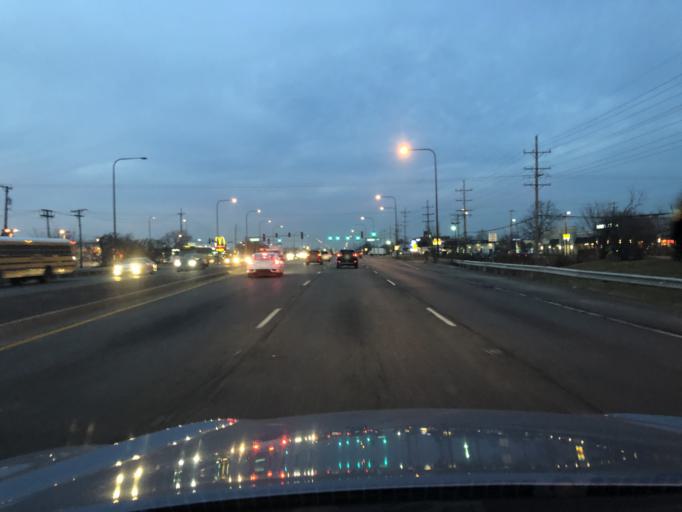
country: US
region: Illinois
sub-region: Cook County
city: Elk Grove Village
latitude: 42.0024
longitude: -87.9594
